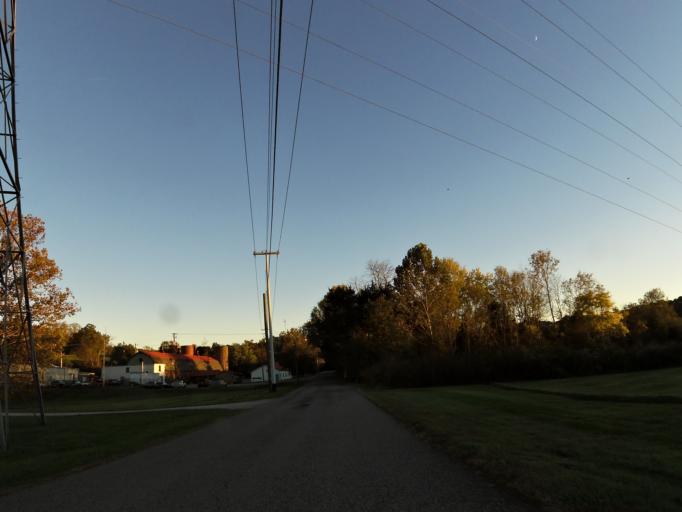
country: US
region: Tennessee
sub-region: Knox County
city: Knoxville
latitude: 36.0324
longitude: -83.9753
